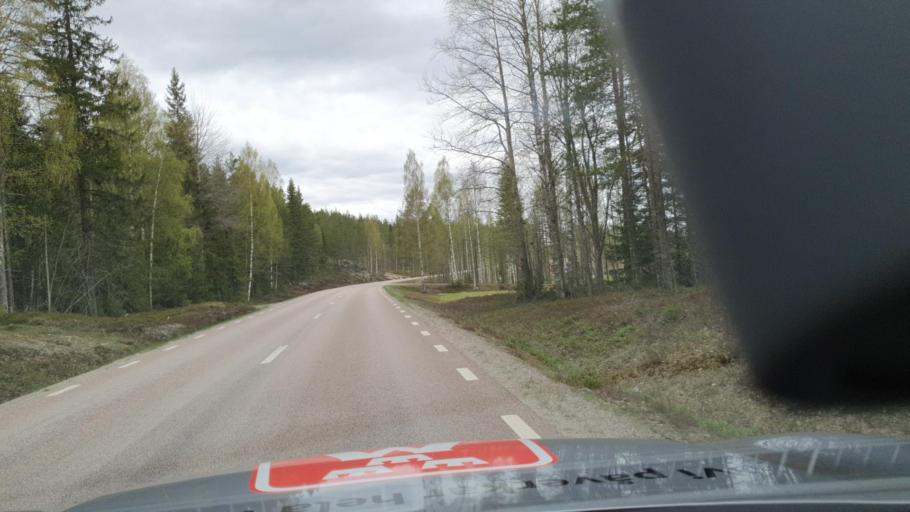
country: SE
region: Vaesternorrland
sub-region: OErnskoeldsviks Kommun
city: Husum
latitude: 63.4650
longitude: 18.9561
